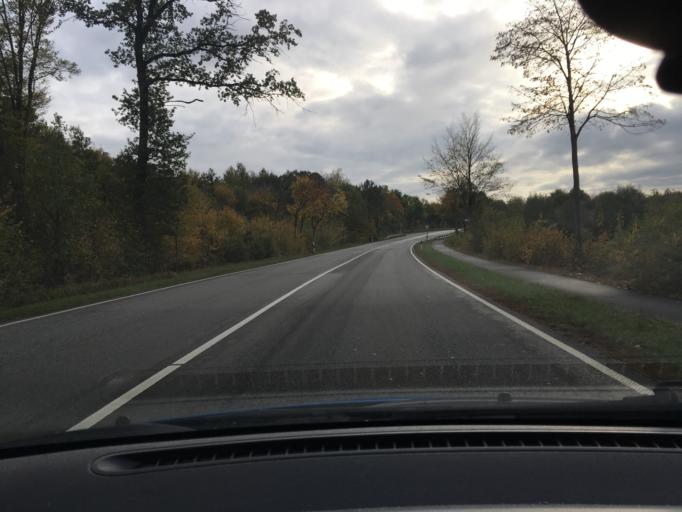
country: DE
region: Schleswig-Holstein
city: Talkau
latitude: 53.5651
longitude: 10.5624
